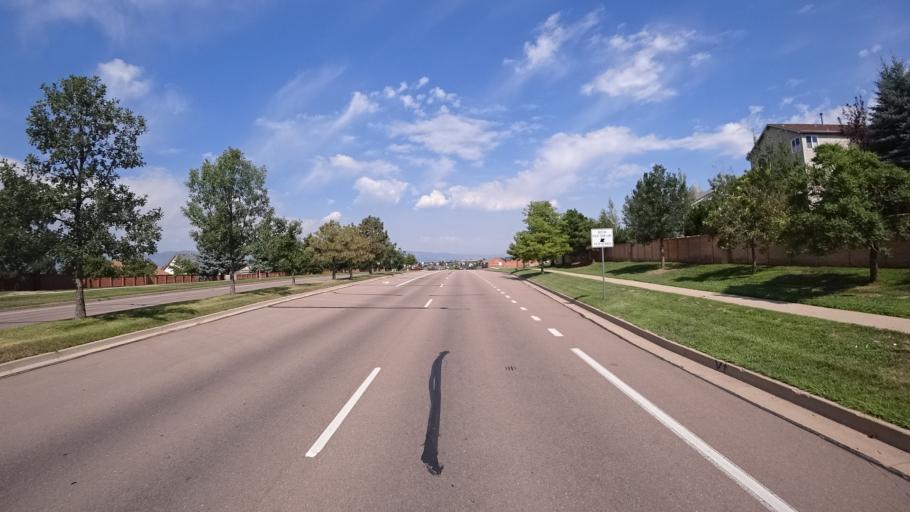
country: US
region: Colorado
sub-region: El Paso County
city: Cimarron Hills
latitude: 38.9300
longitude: -104.7369
